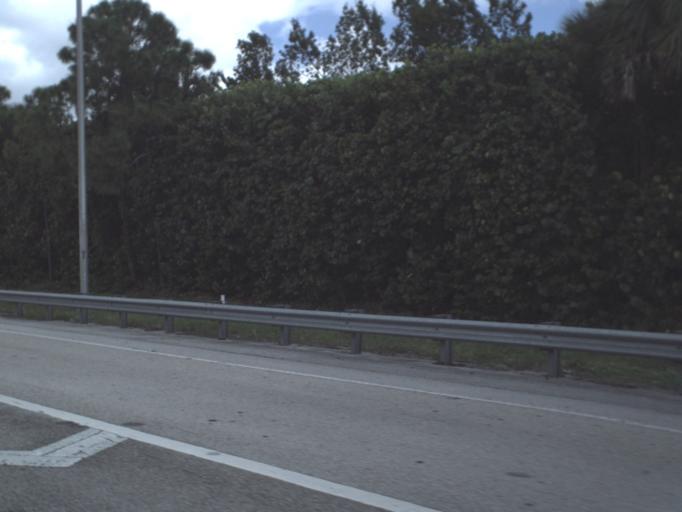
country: US
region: Florida
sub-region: Palm Beach County
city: Greenacres City
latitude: 26.6230
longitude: -80.1737
